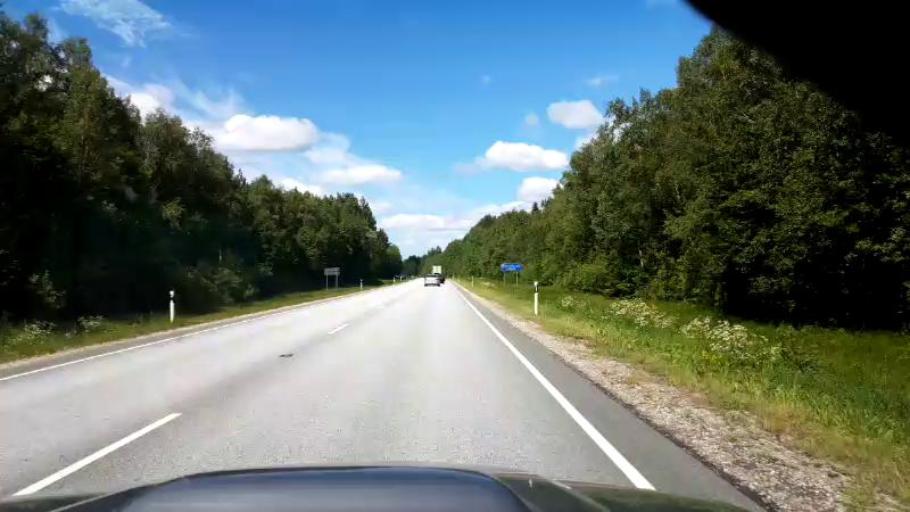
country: EE
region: Paernumaa
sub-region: Halinga vald
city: Parnu-Jaagupi
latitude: 58.5494
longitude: 24.5356
